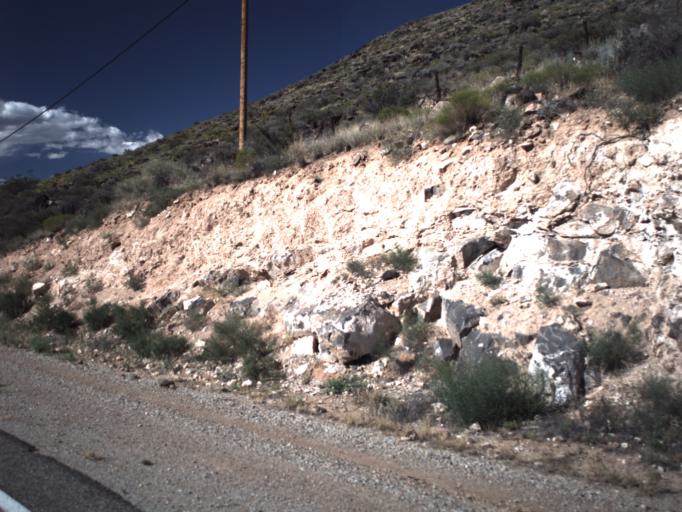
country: US
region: Utah
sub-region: Washington County
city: Toquerville
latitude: 37.2436
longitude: -113.2829
